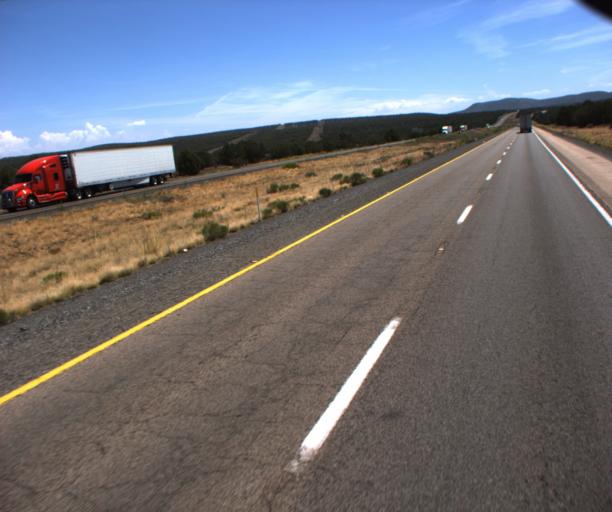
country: US
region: Arizona
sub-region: Mohave County
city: Peach Springs
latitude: 35.1908
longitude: -113.3475
